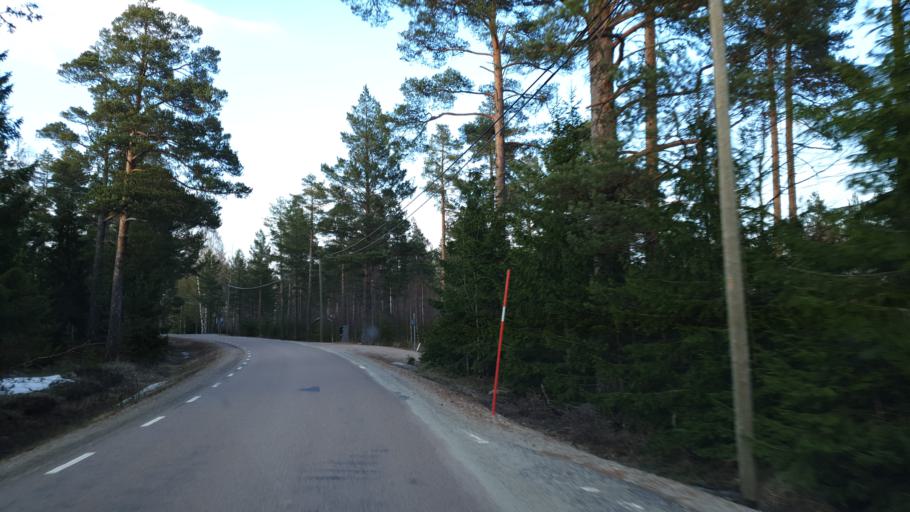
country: SE
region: Vaesternorrland
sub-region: Sundsvalls Kommun
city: Njurundabommen
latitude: 62.2384
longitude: 17.5227
